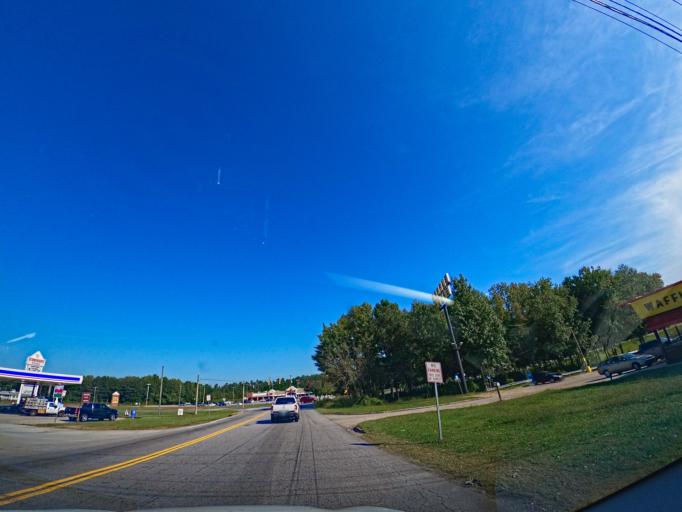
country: US
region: Georgia
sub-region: Troup County
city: Hogansville
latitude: 33.1601
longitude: -84.8721
